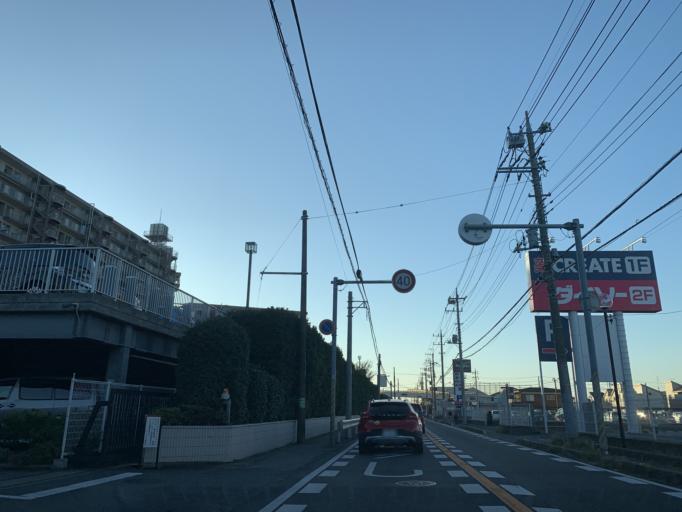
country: JP
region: Chiba
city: Nagareyama
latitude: 35.8866
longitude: 139.9280
